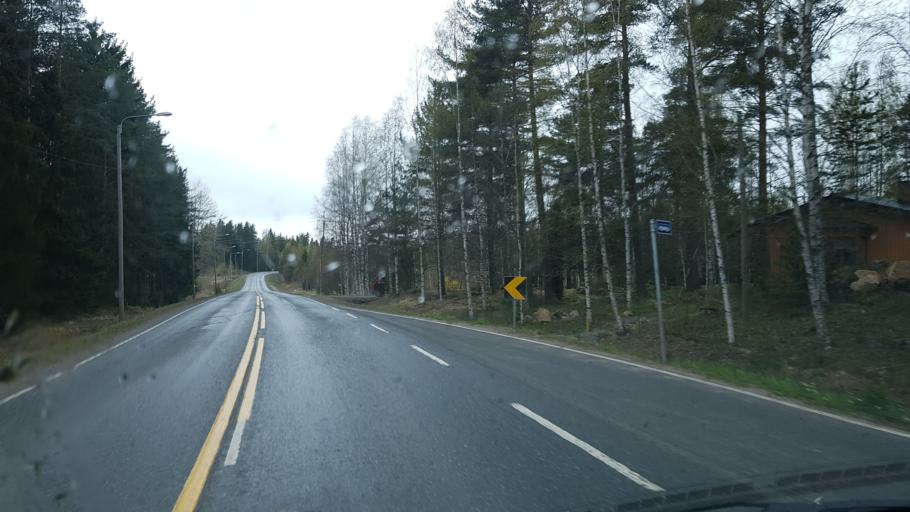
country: FI
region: Pirkanmaa
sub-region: Tampere
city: Pirkkala
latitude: 61.4285
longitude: 23.6295
